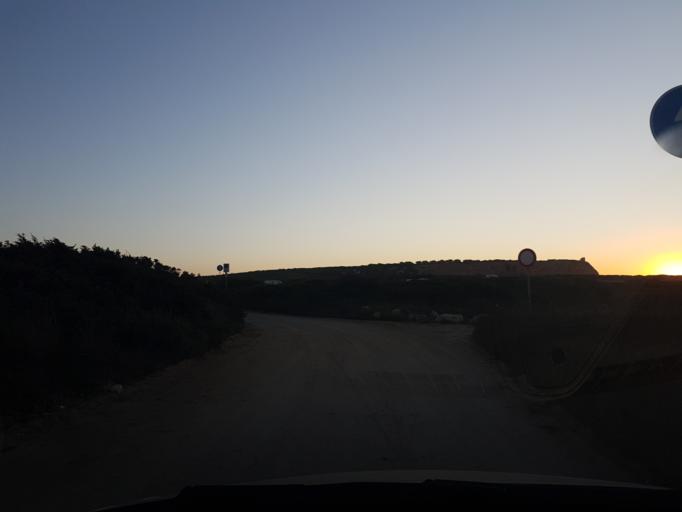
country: IT
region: Sardinia
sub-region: Provincia di Oristano
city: Riola Sardo
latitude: 40.0426
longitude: 8.3991
